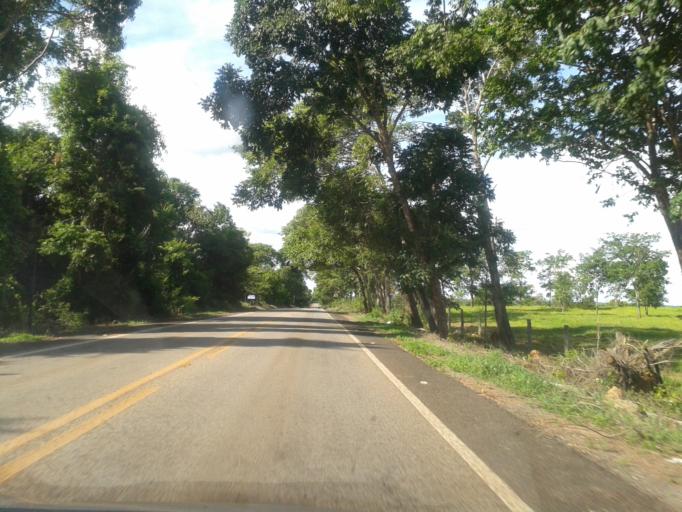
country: BR
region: Goias
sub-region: Mozarlandia
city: Mozarlandia
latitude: -14.6356
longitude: -50.5194
